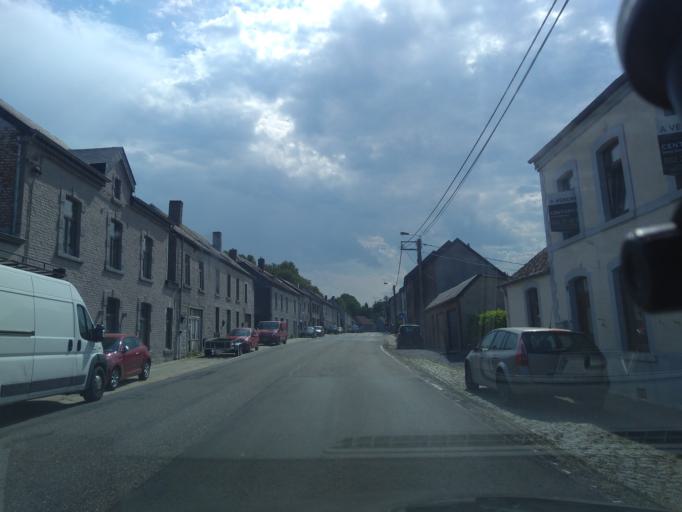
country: BE
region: Wallonia
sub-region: Province de Namur
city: Dinant
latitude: 50.2052
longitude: 4.8964
